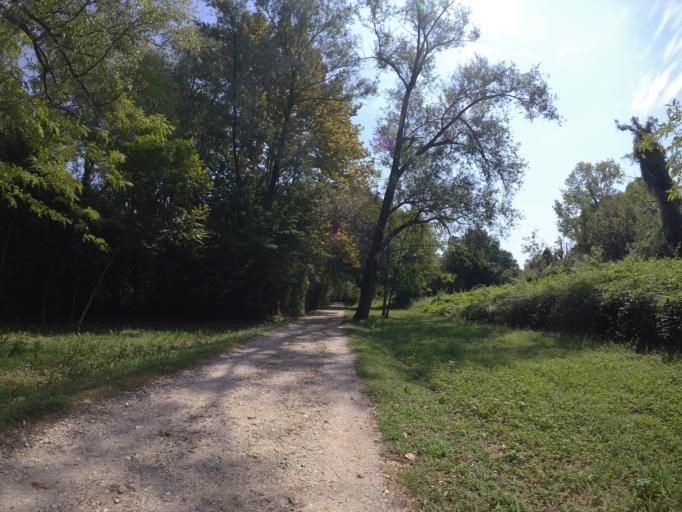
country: IT
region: Friuli Venezia Giulia
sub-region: Provincia di Udine
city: Codroipo
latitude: 45.9509
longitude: 12.9811
